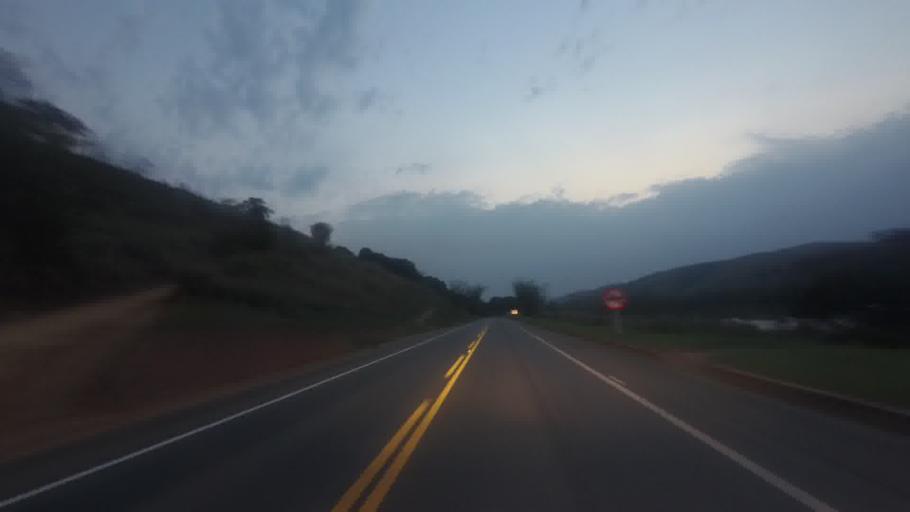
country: BR
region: Minas Gerais
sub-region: Alem Paraiba
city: Alem Paraiba
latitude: -21.9166
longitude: -42.7569
